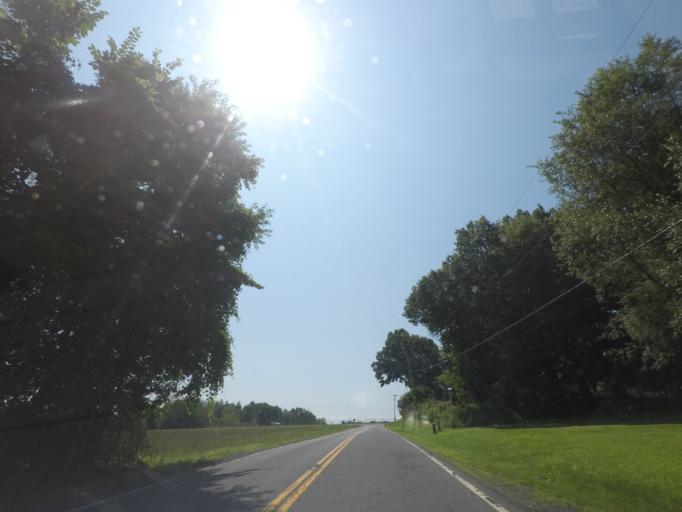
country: US
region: New York
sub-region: Saratoga County
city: Mechanicville
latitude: 42.8537
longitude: -73.7183
